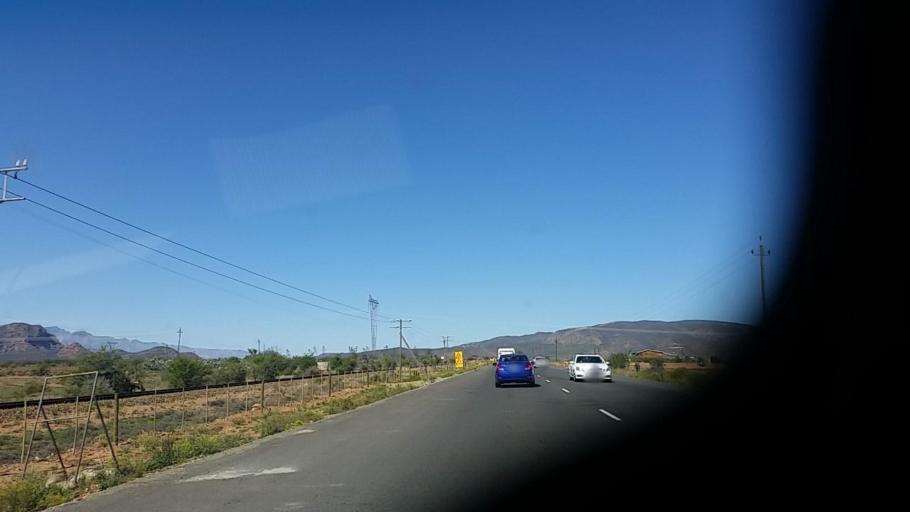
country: ZA
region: Western Cape
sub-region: Eden District Municipality
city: Oudtshoorn
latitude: -33.5609
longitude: 22.3919
